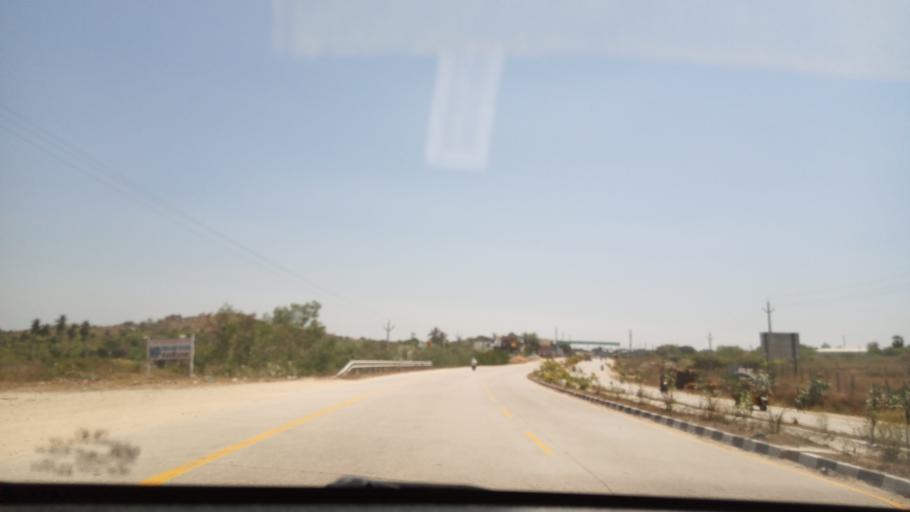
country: IN
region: Andhra Pradesh
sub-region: Chittoor
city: Chittoor
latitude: 13.2048
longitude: 78.9433
